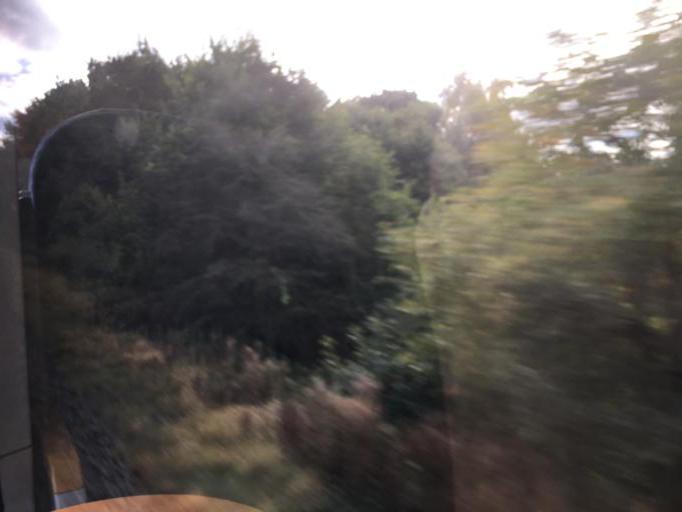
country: DE
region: Schleswig-Holstein
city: Melsdorf
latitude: 54.3098
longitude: 10.0572
